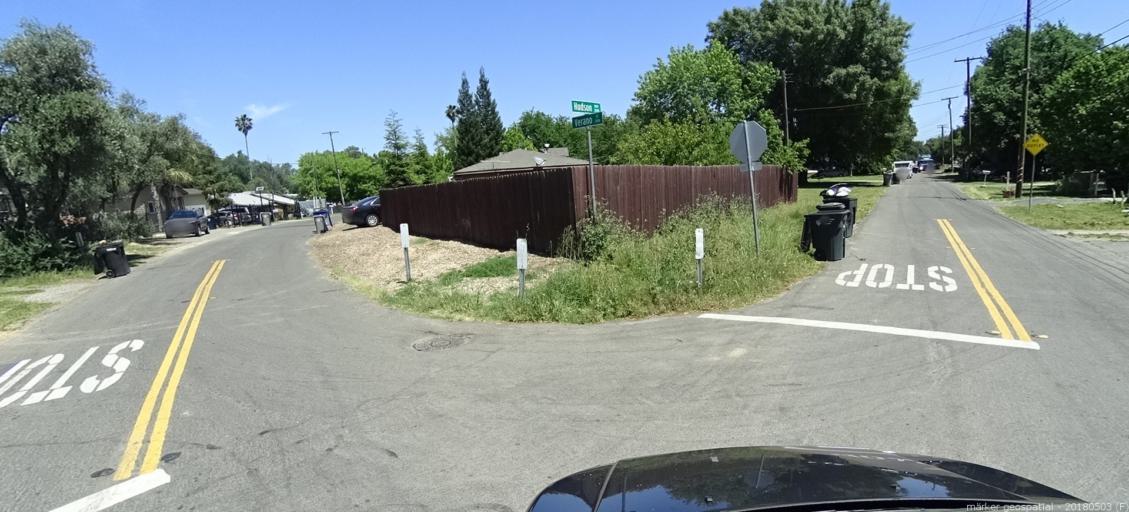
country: US
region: California
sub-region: Sacramento County
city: Arden-Arcade
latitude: 38.6279
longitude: -121.4195
